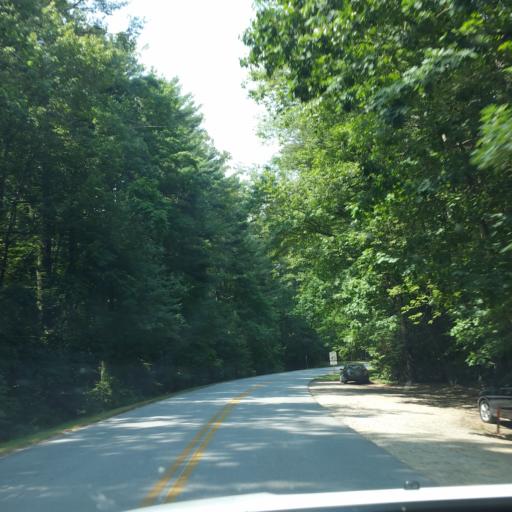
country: US
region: North Carolina
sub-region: Buncombe County
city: Biltmore Forest
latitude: 35.5177
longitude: -82.5300
